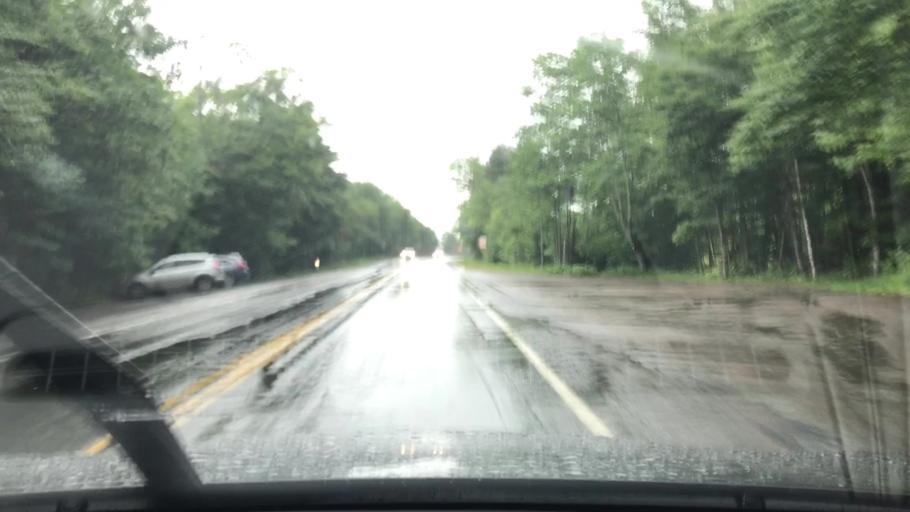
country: US
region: Vermont
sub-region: Lamoille County
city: Johnson
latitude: 44.5185
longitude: -72.7698
